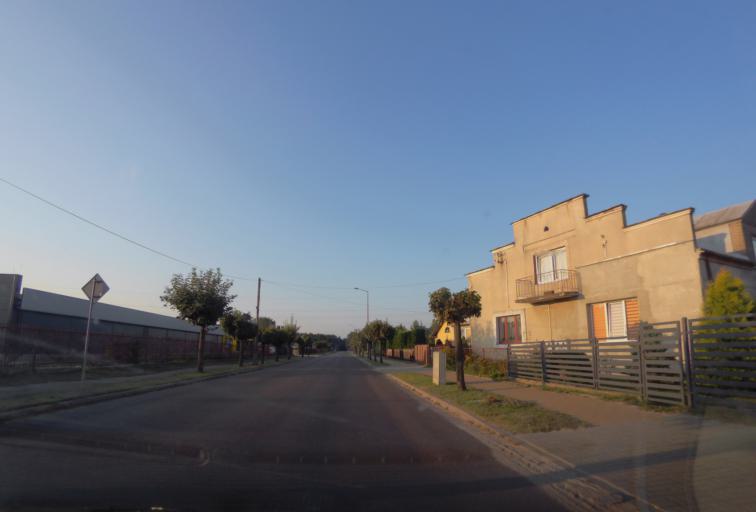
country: PL
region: Lublin Voivodeship
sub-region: Powiat janowski
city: Janow Lubelski
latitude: 50.6984
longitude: 22.4205
